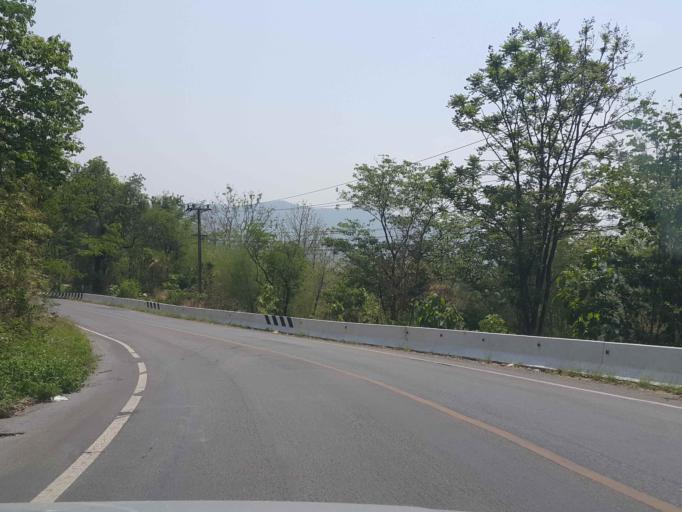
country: TH
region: Chiang Mai
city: Mae On
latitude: 18.8305
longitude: 99.2602
